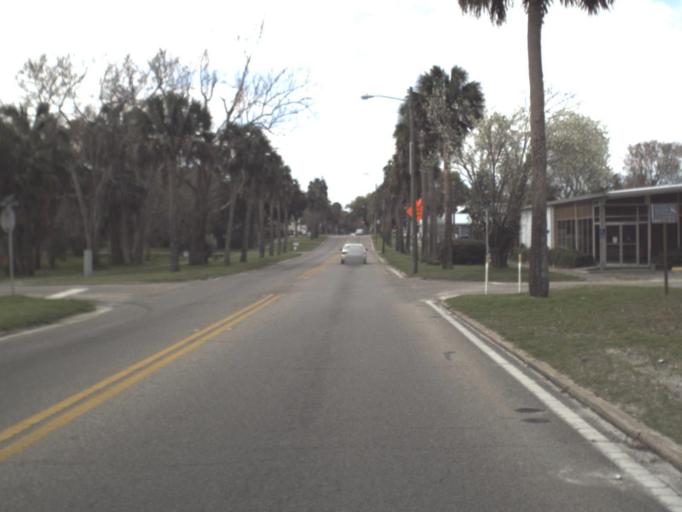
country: US
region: Florida
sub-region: Franklin County
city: Apalachicola
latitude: 29.7248
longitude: -84.9878
